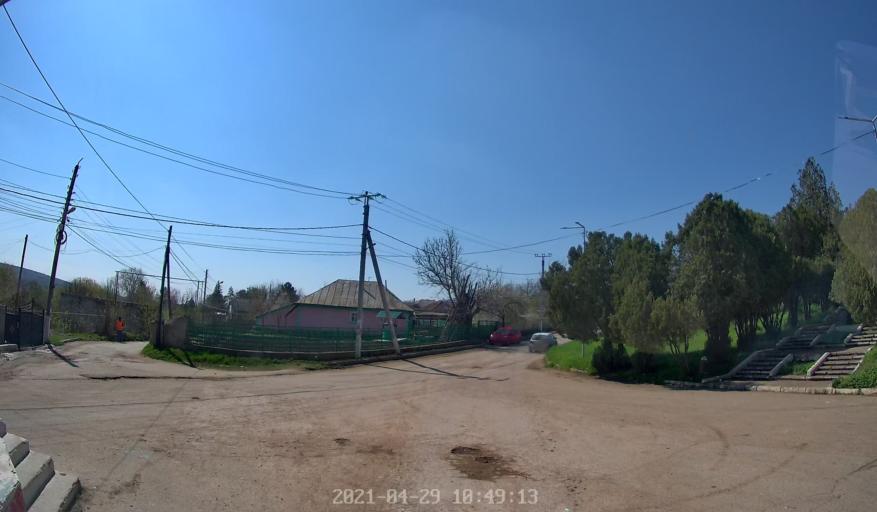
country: MD
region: Chisinau
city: Ciorescu
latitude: 47.1681
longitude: 28.9504
